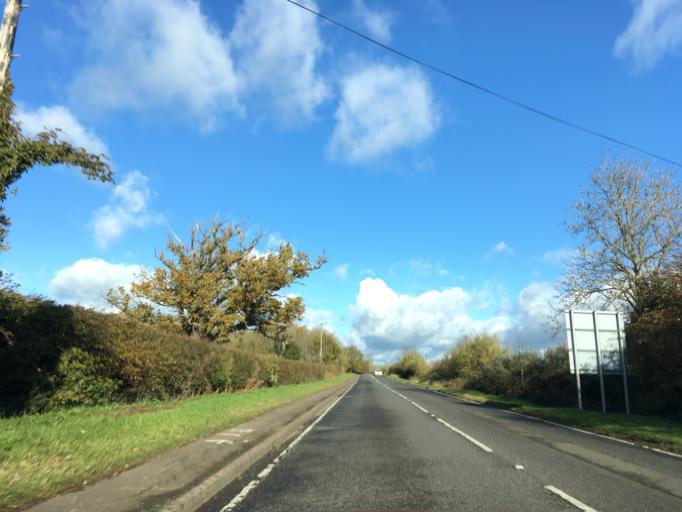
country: GB
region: England
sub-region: Warwickshire
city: Bidford-on-avon
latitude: 52.1834
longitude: -1.9013
